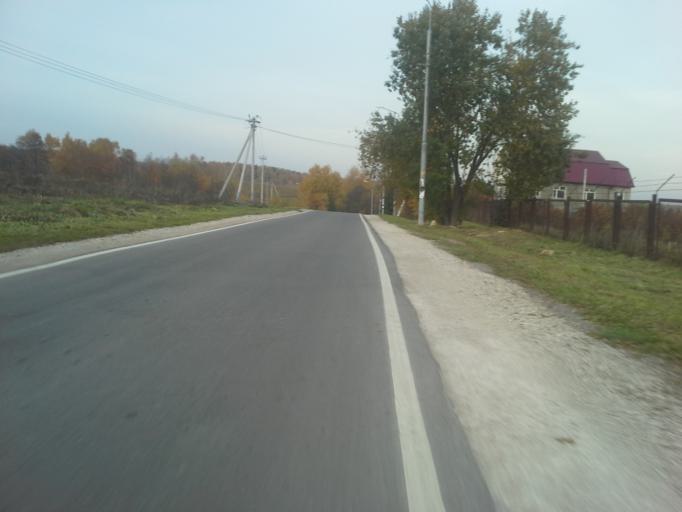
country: RU
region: Moskovskaya
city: Dubrovitsy
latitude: 55.4932
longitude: 37.4274
